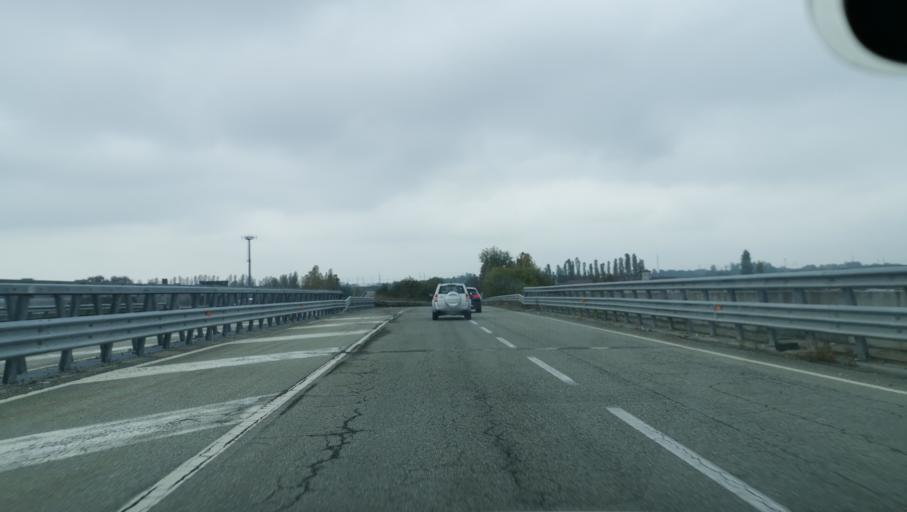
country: IT
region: Piedmont
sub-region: Provincia di Torino
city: Brandizzo
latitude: 45.1676
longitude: 7.8143
